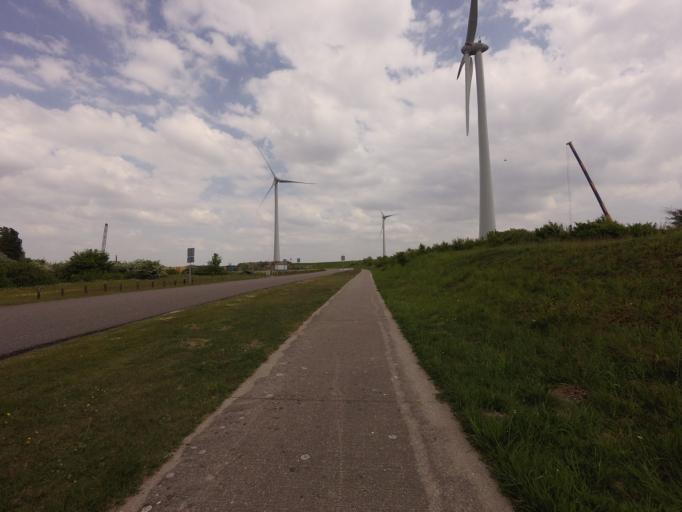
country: NL
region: Zeeland
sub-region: Schouwen-Duiveland
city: Bruinisse
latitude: 51.6786
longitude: 4.1451
